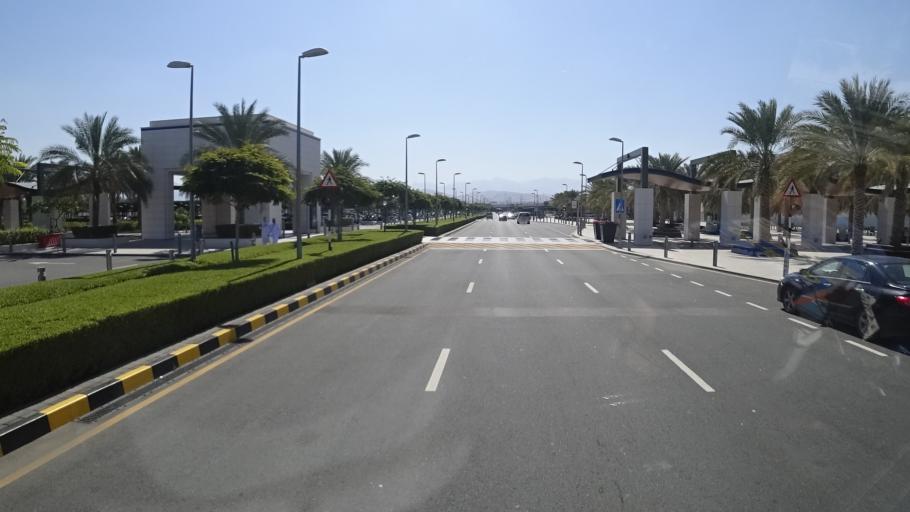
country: OM
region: Muhafazat Masqat
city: Bawshar
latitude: 23.6018
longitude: 58.2920
